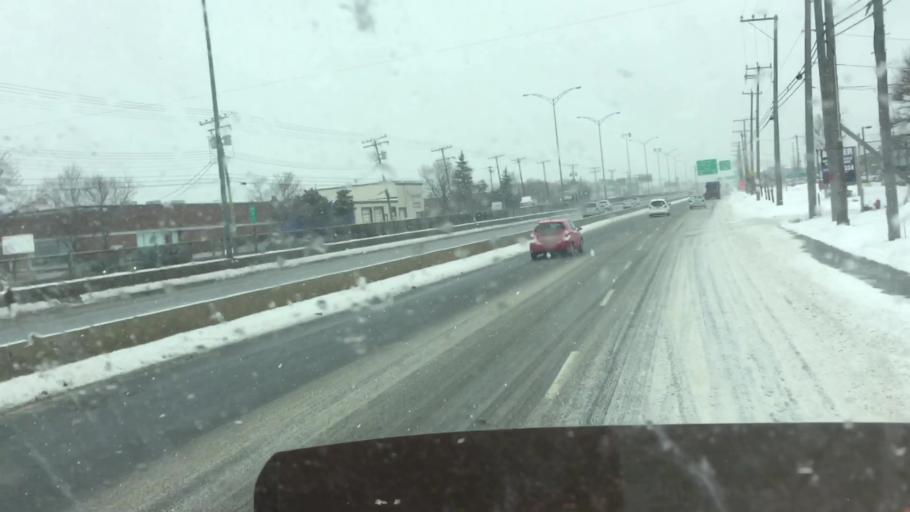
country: CA
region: Quebec
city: Cote-Saint-Luc
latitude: 45.4707
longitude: -73.7113
